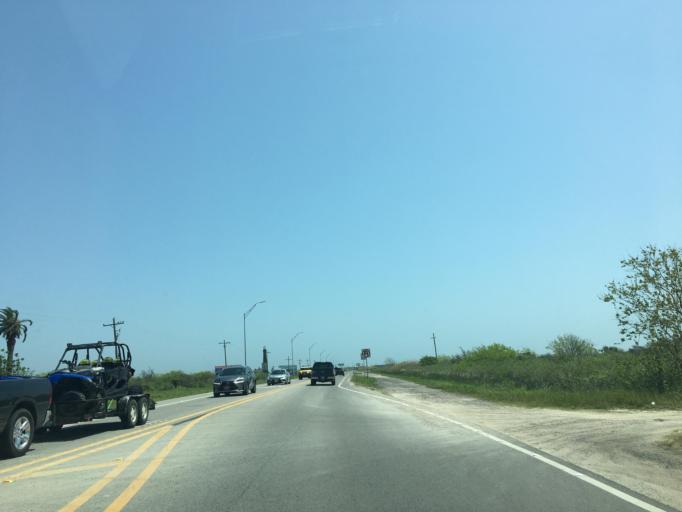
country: US
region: Texas
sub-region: Galveston County
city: Galveston
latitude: 29.3645
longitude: -94.7741
